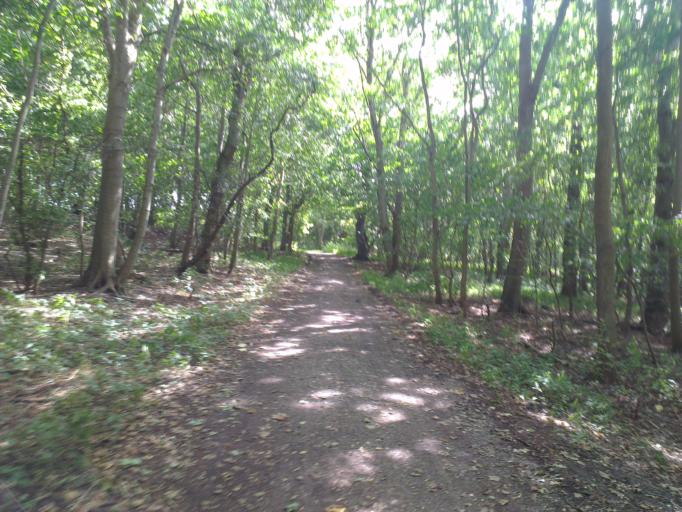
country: DK
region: Capital Region
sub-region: Frederikssund Kommune
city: Jaegerspris
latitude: 55.8534
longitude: 11.9613
